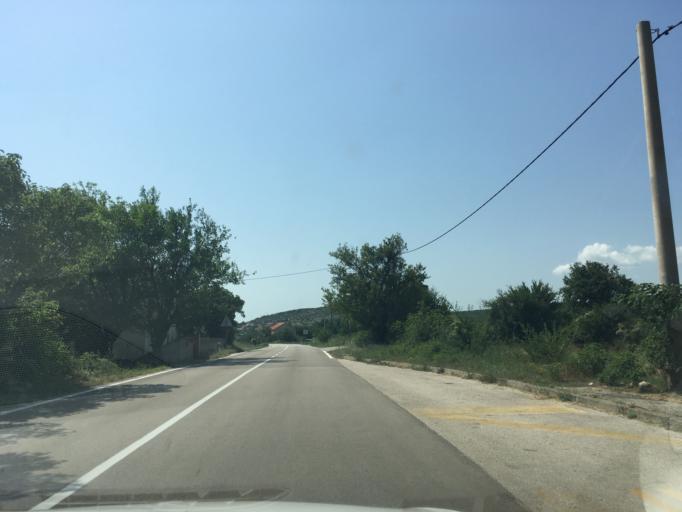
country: HR
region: Zadarska
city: Benkovac
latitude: 43.9621
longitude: 15.7646
